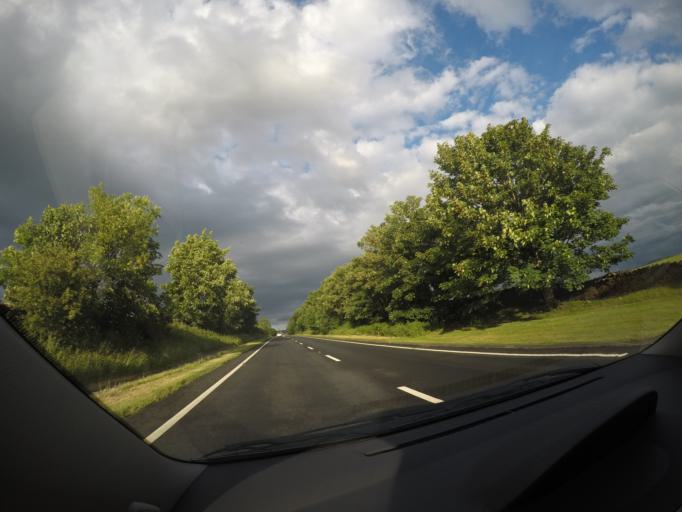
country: GB
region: England
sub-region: Cumbria
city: Penrith
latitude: 54.6534
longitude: -2.6829
